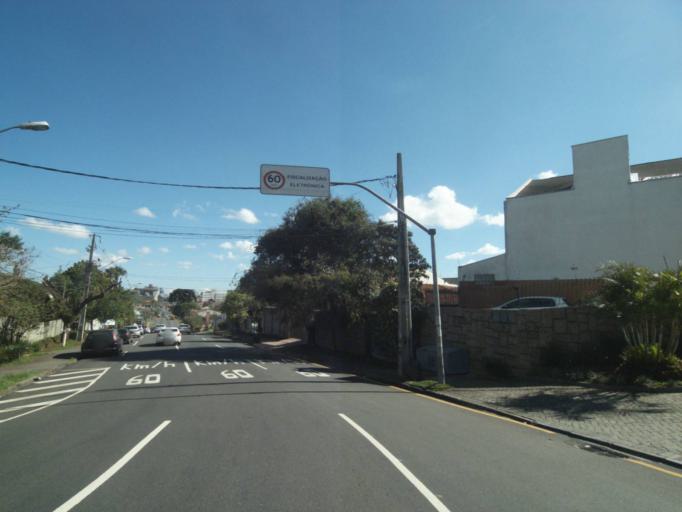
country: BR
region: Parana
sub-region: Curitiba
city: Curitiba
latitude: -25.3951
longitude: -49.2581
